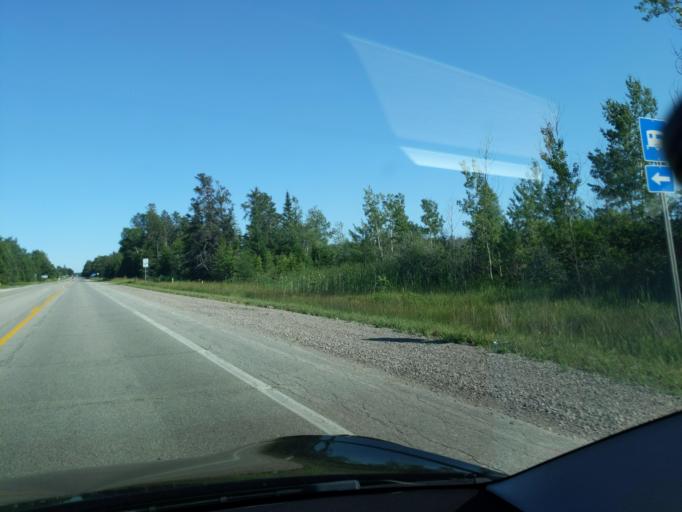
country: US
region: Michigan
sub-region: Mackinac County
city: Saint Ignace
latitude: 45.7640
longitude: -84.7175
